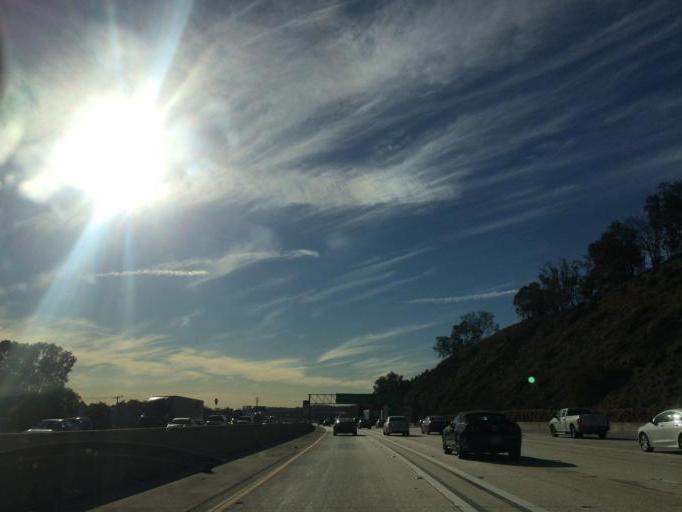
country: US
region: California
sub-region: Los Angeles County
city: La Verne
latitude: 34.0719
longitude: -117.7921
